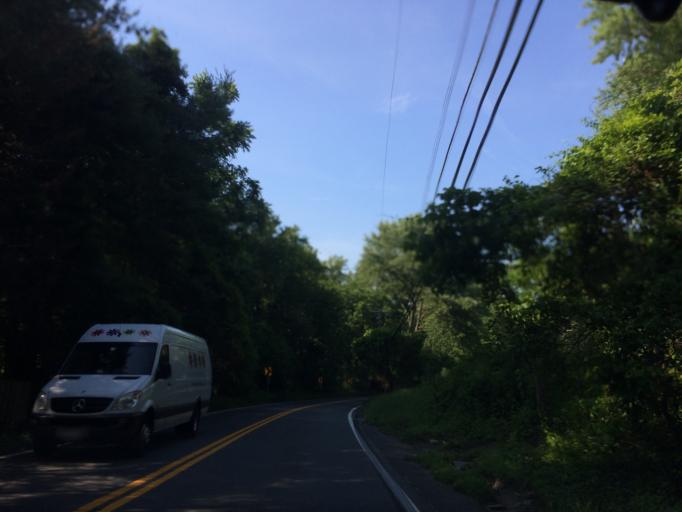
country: US
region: Maryland
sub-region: Montgomery County
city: Olney
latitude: 39.2067
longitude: -77.0636
